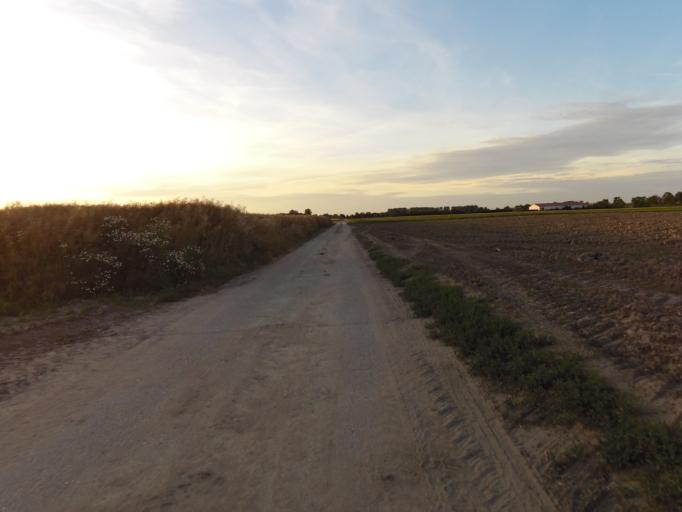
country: DE
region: Rheinland-Pfalz
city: Beindersheim
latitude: 49.5723
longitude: 8.3346
